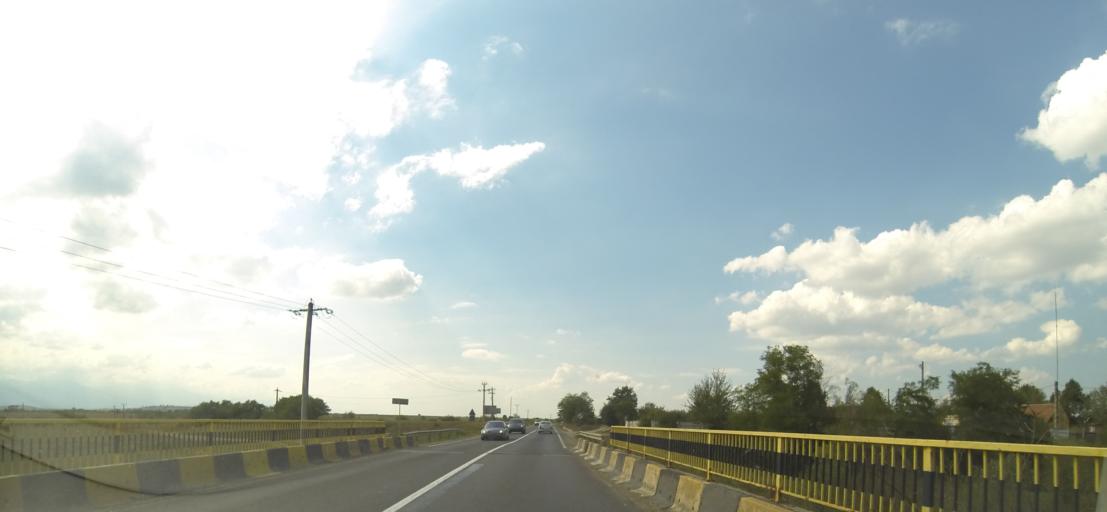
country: RO
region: Brasov
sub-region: Comuna Sercaia
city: Sercaia
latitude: 45.8303
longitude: 25.1350
